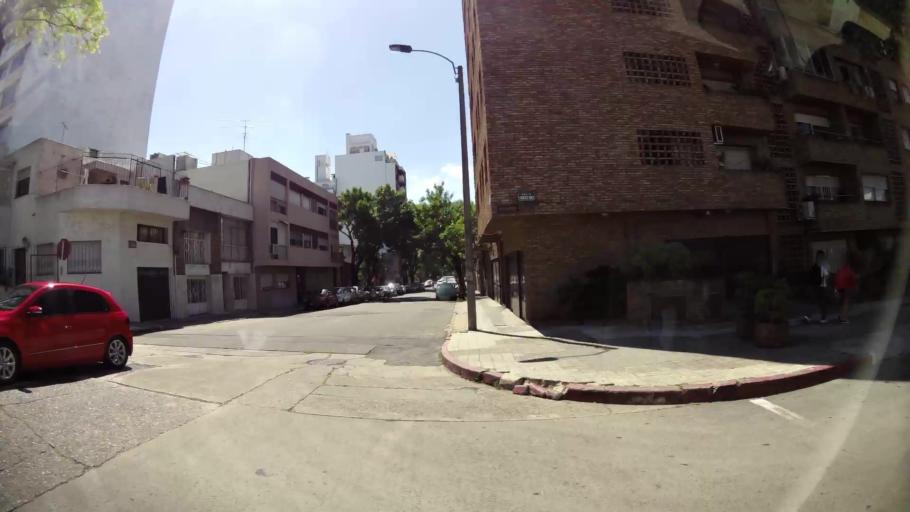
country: UY
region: Montevideo
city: Montevideo
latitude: -34.9064
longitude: -56.1491
